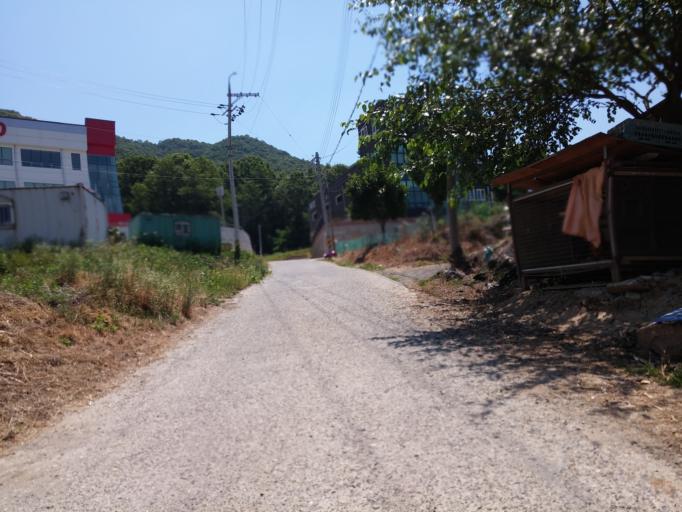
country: KR
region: Chungcheongbuk-do
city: Cheongju-si
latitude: 36.5557
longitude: 127.4380
